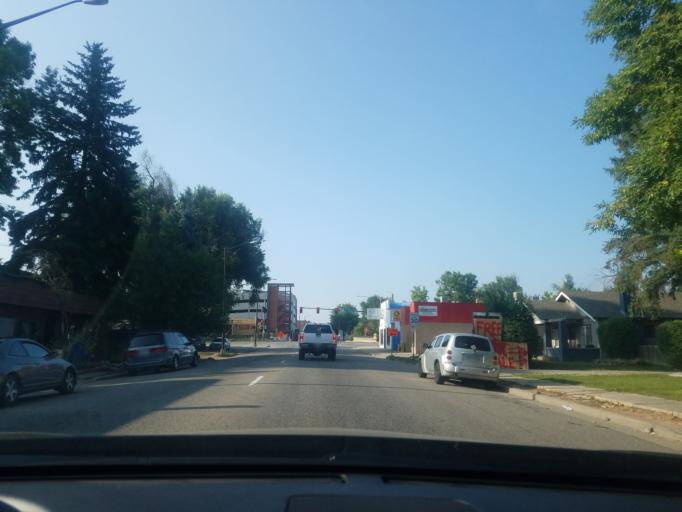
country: US
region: Colorado
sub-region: Larimer County
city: Loveland
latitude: 40.3919
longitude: -105.0732
